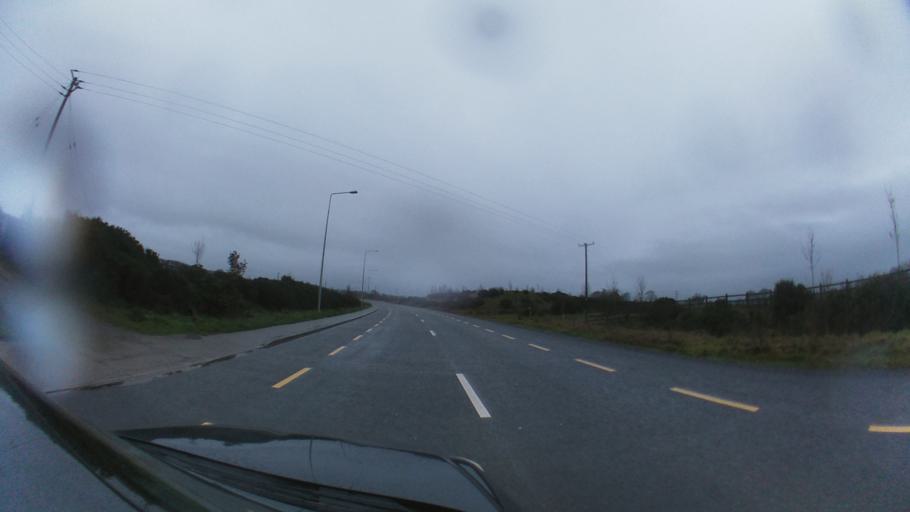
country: IE
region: Leinster
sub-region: County Carlow
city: Bagenalstown
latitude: 52.6757
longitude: -7.0299
